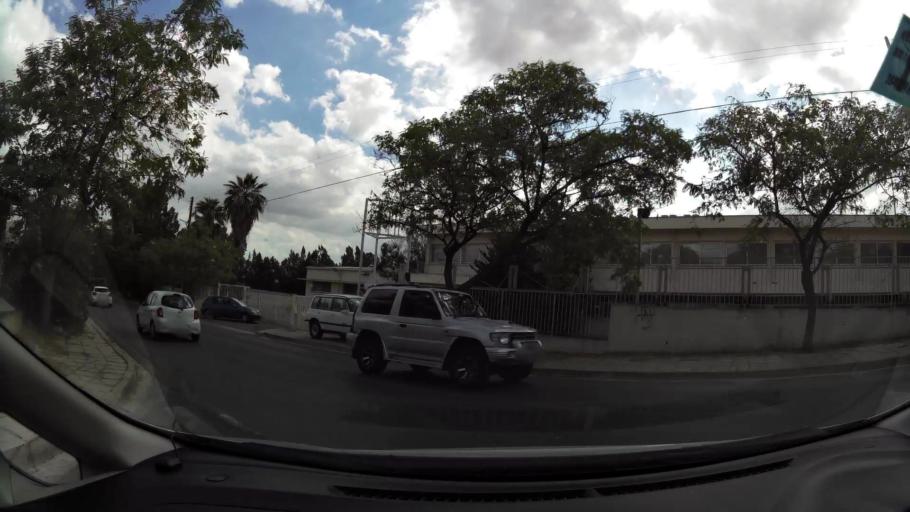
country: CY
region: Lefkosia
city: Nicosia
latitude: 35.1791
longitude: 33.3902
